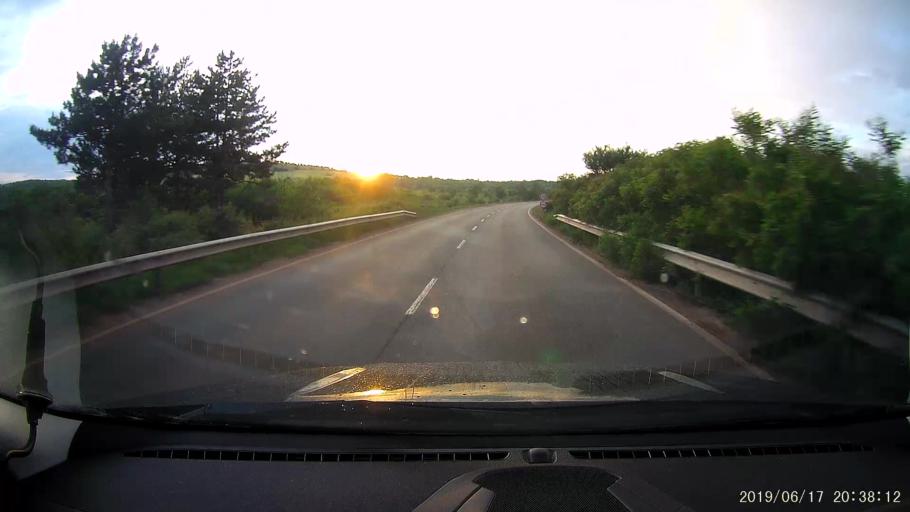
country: BG
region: Sofiya
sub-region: Obshtina Slivnitsa
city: Slivnitsa
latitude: 42.8692
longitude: 23.0208
